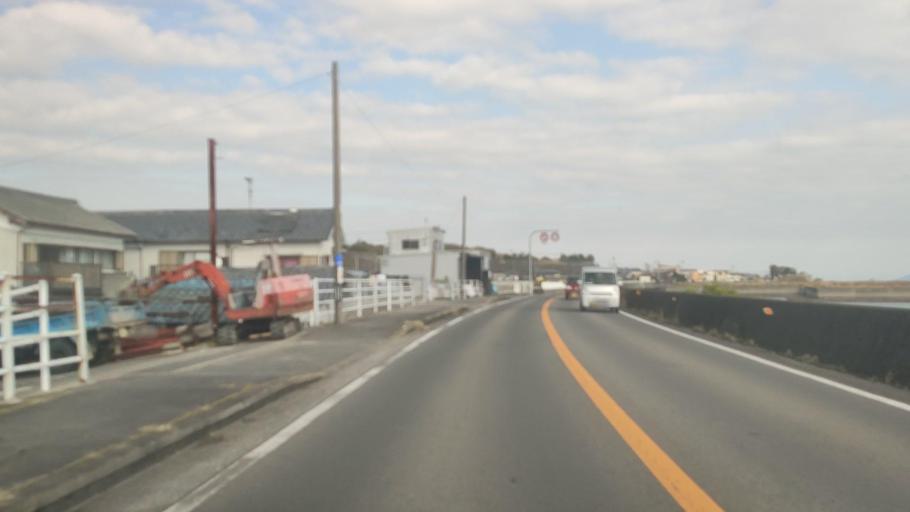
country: JP
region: Nagasaki
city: Shimabara
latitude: 32.6699
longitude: 130.3331
